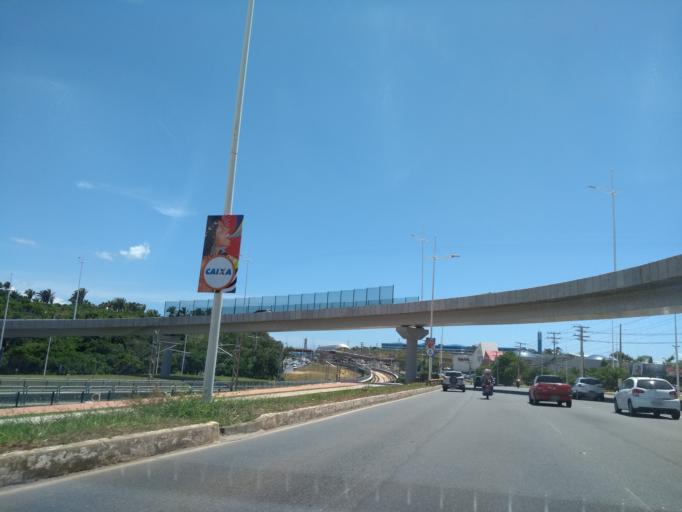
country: BR
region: Bahia
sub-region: Lauro De Freitas
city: Lauro de Freitas
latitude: -12.9373
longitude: -38.3989
